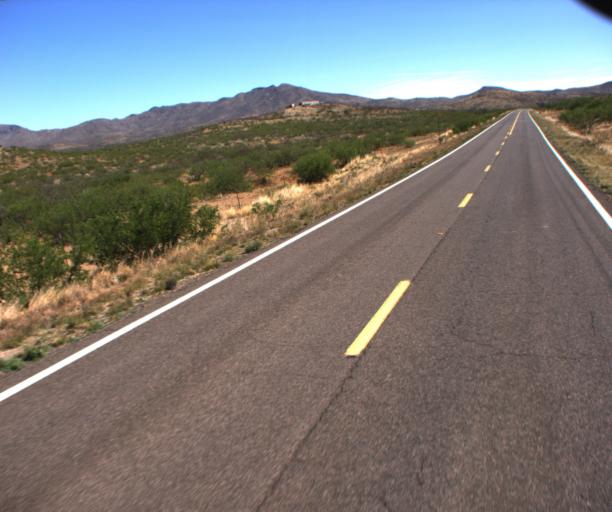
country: US
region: Arizona
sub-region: Cochise County
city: Douglas
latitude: 31.4877
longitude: -109.4364
